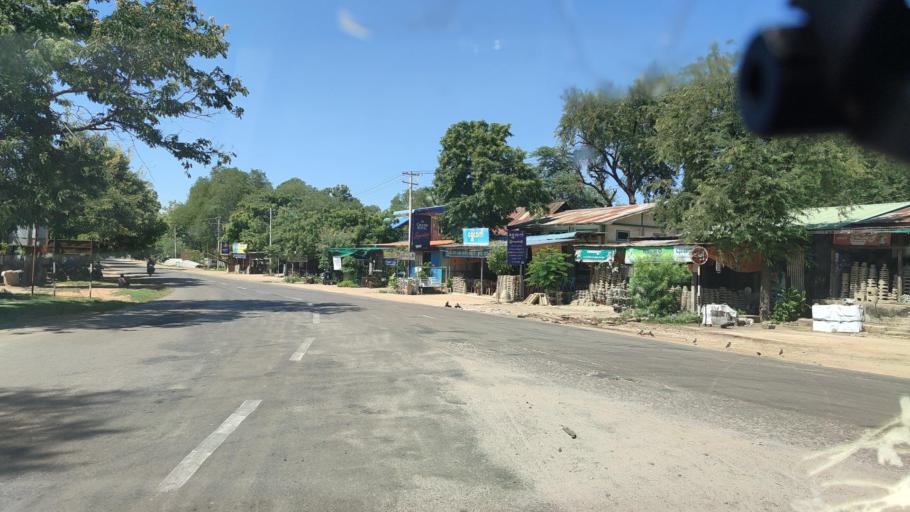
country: MM
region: Magway
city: Chauk
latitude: 20.8008
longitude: 95.0187
